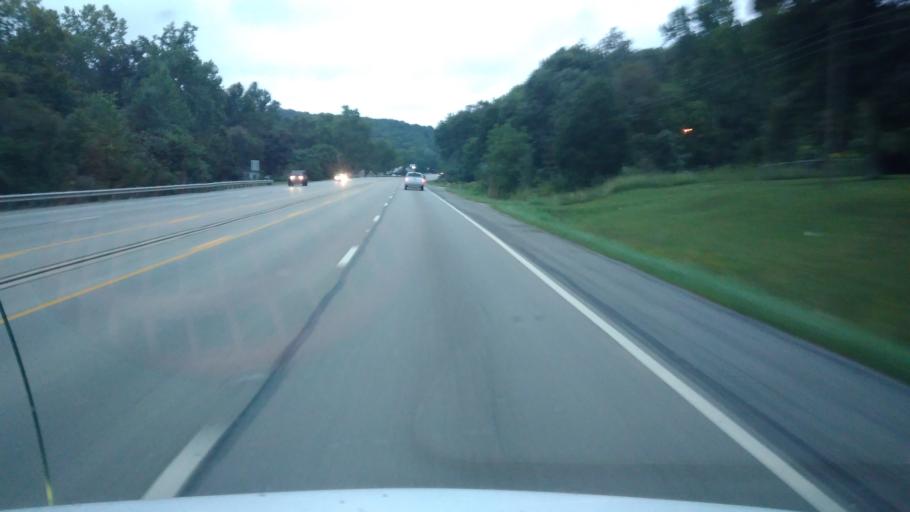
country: US
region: Ohio
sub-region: Ross County
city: Chillicothe
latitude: 39.2300
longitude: -82.9840
